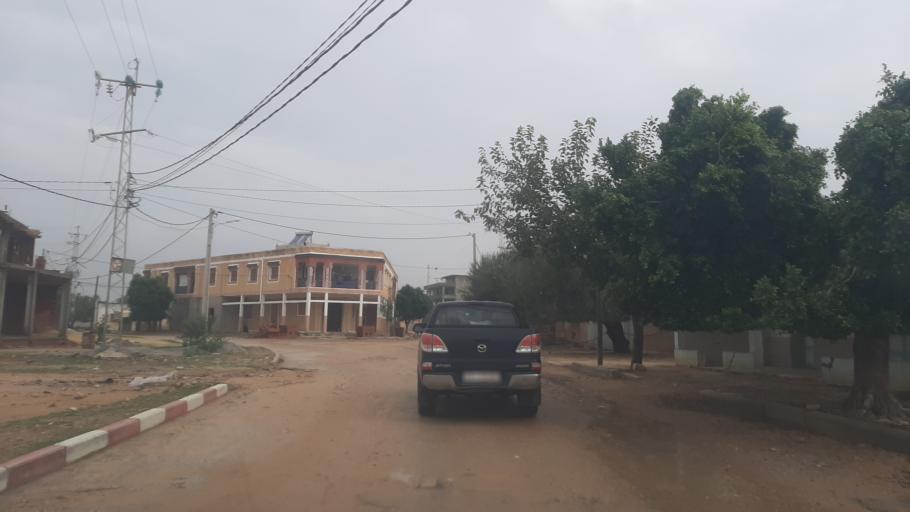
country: TN
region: Al Munastir
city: Sidi Bin Nur
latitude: 35.4813
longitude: 10.8731
